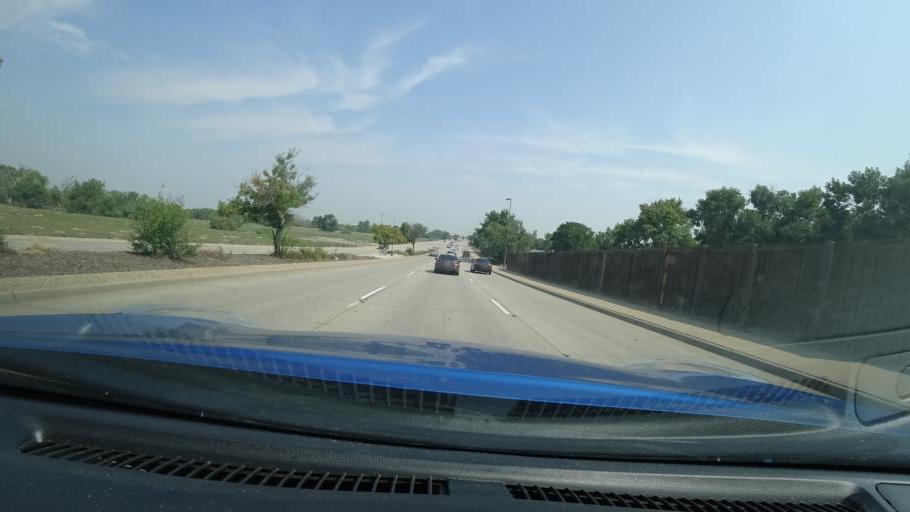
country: US
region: Colorado
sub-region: Adams County
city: Aurora
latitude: 39.7425
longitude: -104.7913
